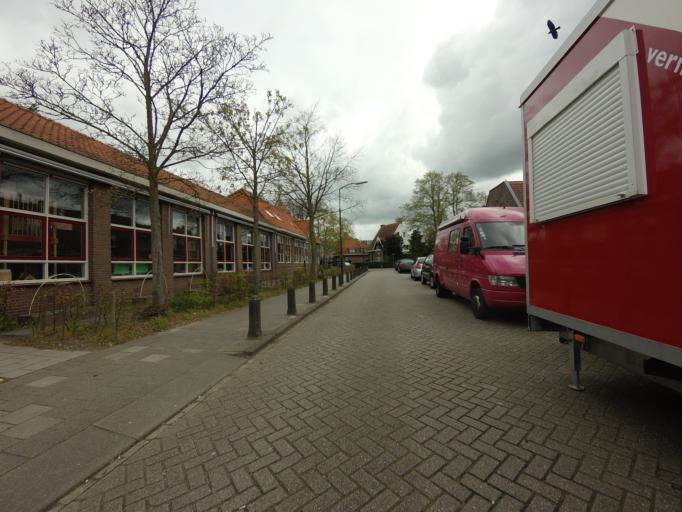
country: NL
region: North Holland
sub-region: Gemeente Amsterdam
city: Amsterdam-Zuidoost
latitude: 52.2693
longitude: 4.9709
